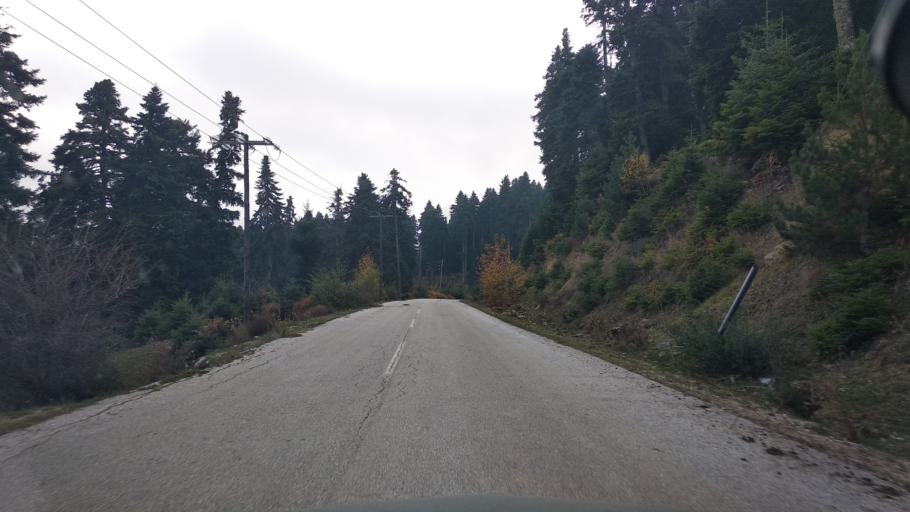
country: GR
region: Thessaly
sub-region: Trikala
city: Pyli
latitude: 39.5783
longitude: 21.4924
